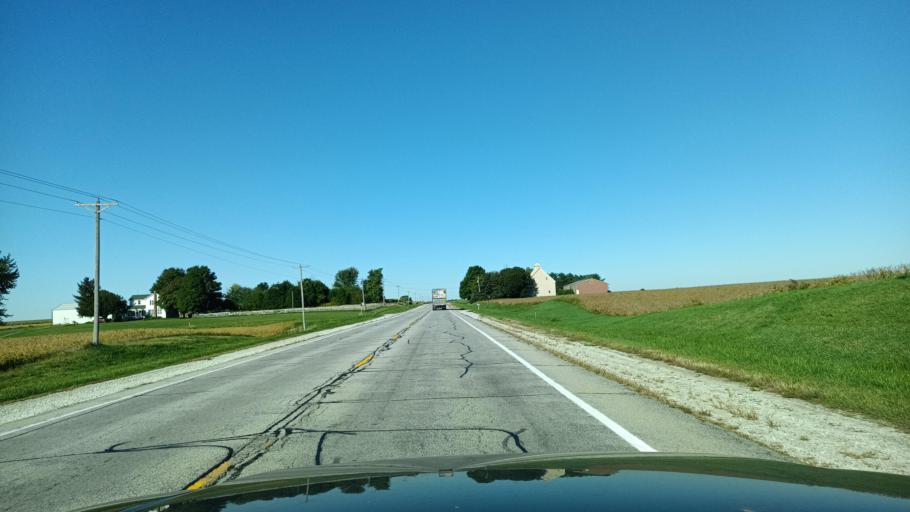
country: US
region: Illinois
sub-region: Warren County
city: Monmouth
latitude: 40.8785
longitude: -90.7089
